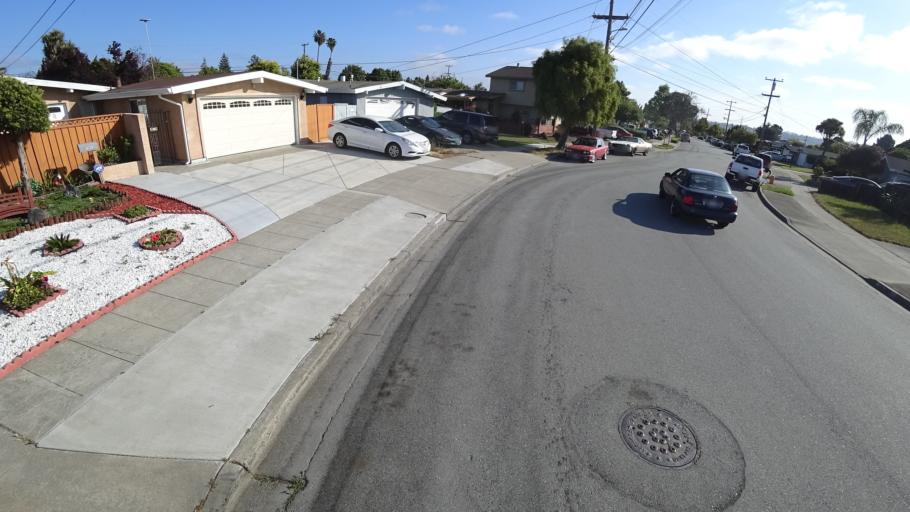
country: US
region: California
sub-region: Alameda County
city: Hayward
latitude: 37.6358
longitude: -122.0979
